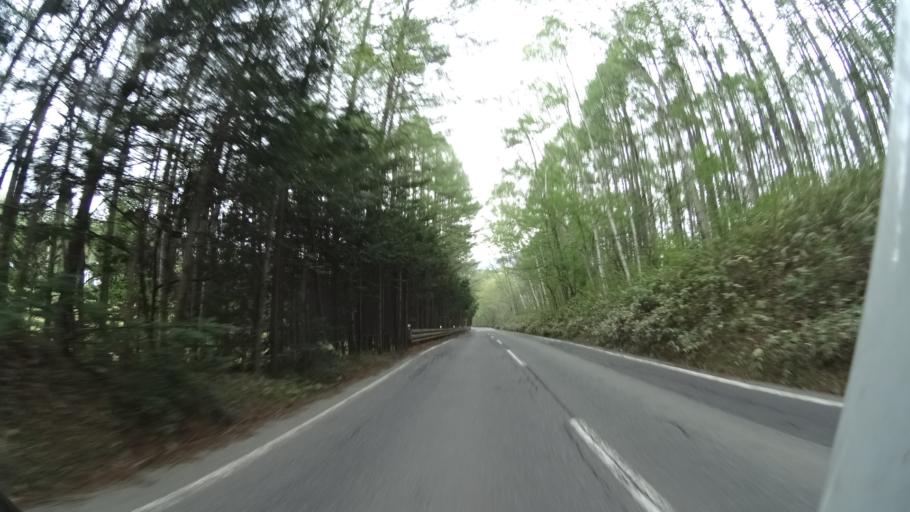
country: JP
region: Nagano
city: Nagano-shi
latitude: 36.7064
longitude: 138.1331
